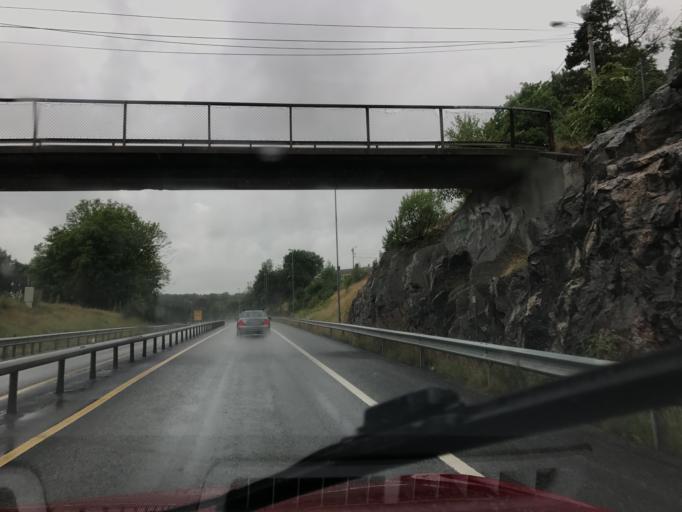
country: NO
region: Aust-Agder
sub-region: Grimstad
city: Grimstad
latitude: 58.3510
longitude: 8.5920
